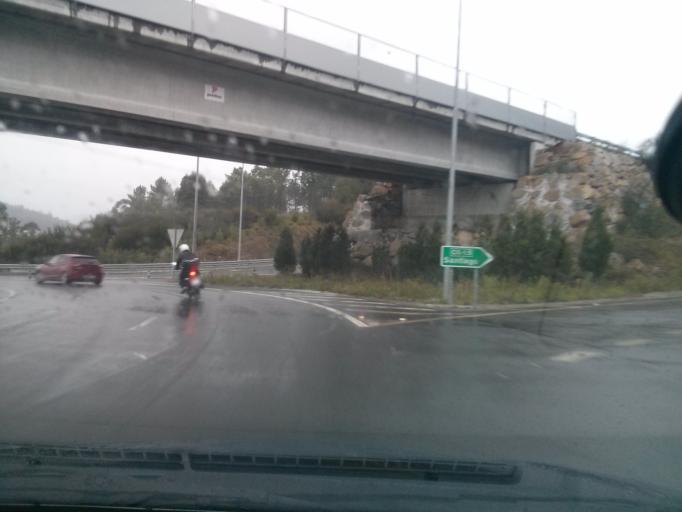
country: ES
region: Galicia
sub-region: Provincia da Coruna
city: Noia
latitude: 42.8117
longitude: -8.8844
